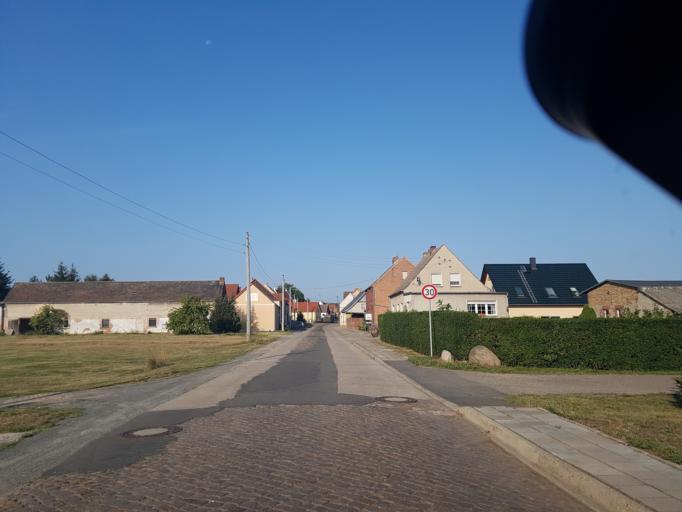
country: DE
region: Saxony-Anhalt
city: Kropstadt
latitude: 51.9654
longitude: 12.7501
